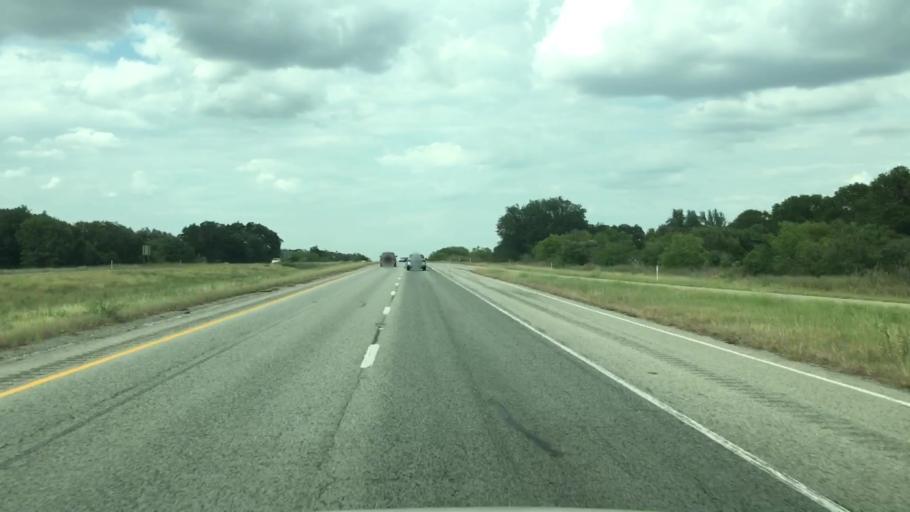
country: US
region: Texas
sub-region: Atascosa County
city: Pleasanton
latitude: 29.0548
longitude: -98.4321
